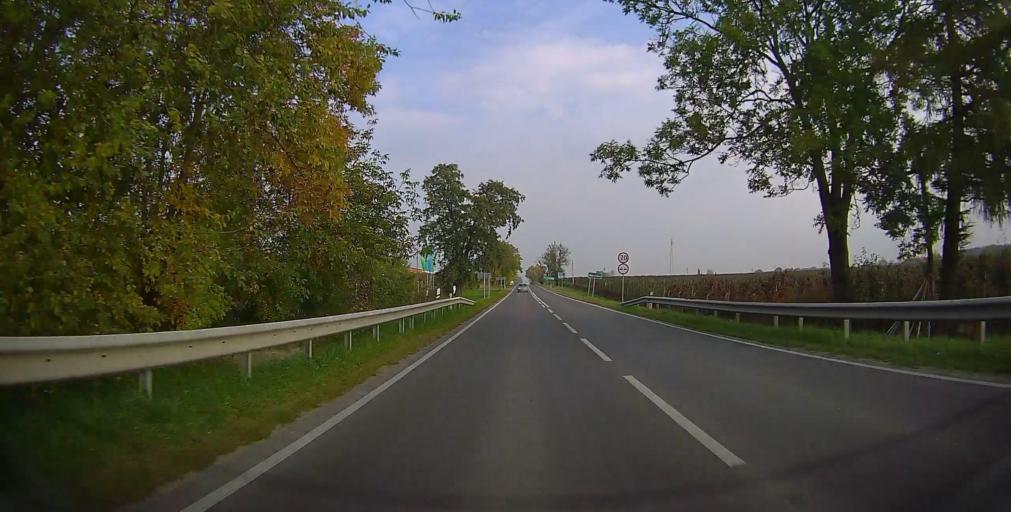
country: PL
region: Masovian Voivodeship
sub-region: Powiat grojecki
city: Mogielnica
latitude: 51.7314
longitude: 20.7523
